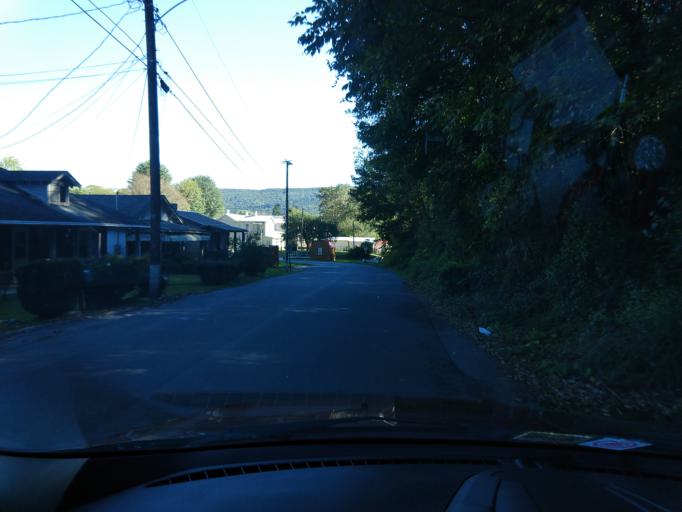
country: US
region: Virginia
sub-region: Alleghany County
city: Clifton Forge
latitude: 37.8243
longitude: -79.8305
